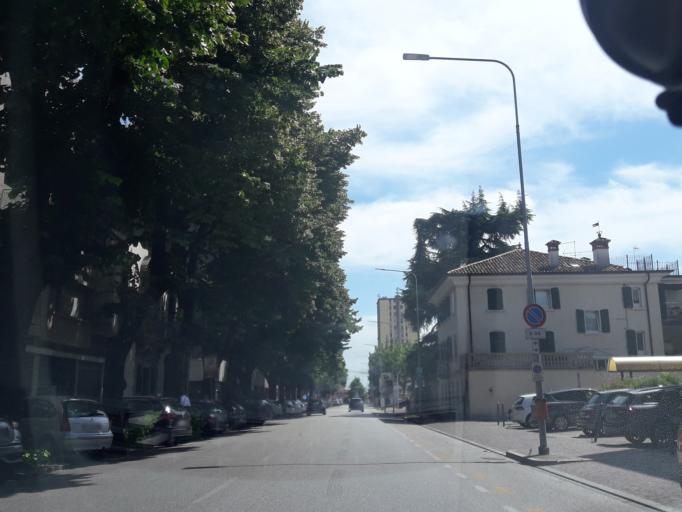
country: IT
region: Friuli Venezia Giulia
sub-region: Provincia di Udine
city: Udine
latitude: 46.0579
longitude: 13.2289
